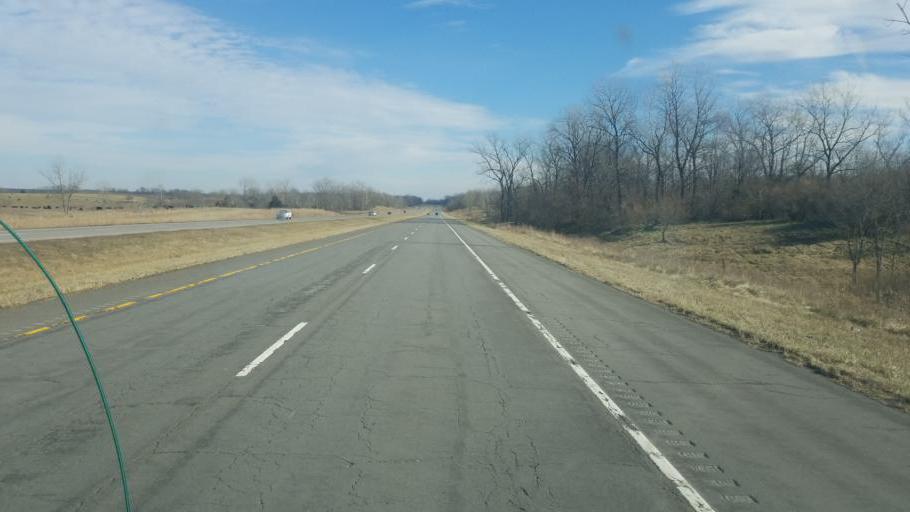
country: US
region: Illinois
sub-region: Saline County
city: Carrier Mills
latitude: 37.7304
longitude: -88.7663
